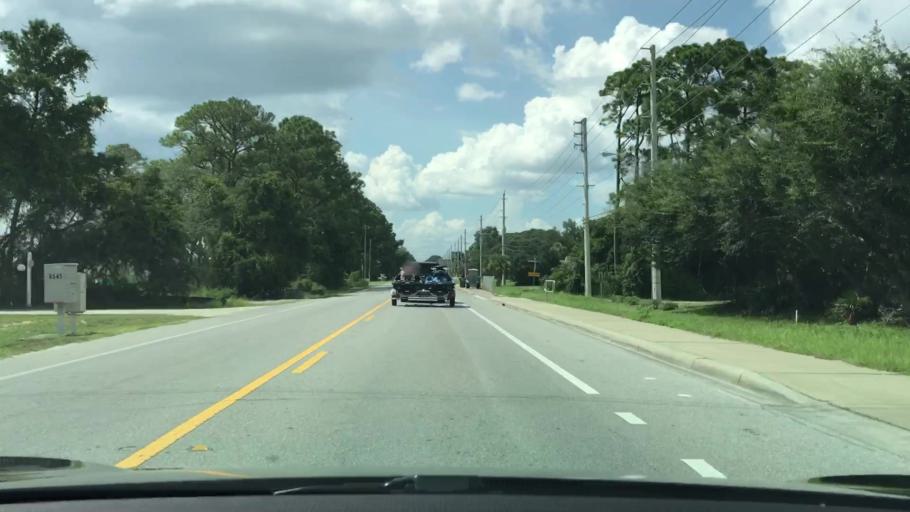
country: US
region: Florida
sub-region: Bay County
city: Lower Grand Lagoon
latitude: 30.1573
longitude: -85.7582
